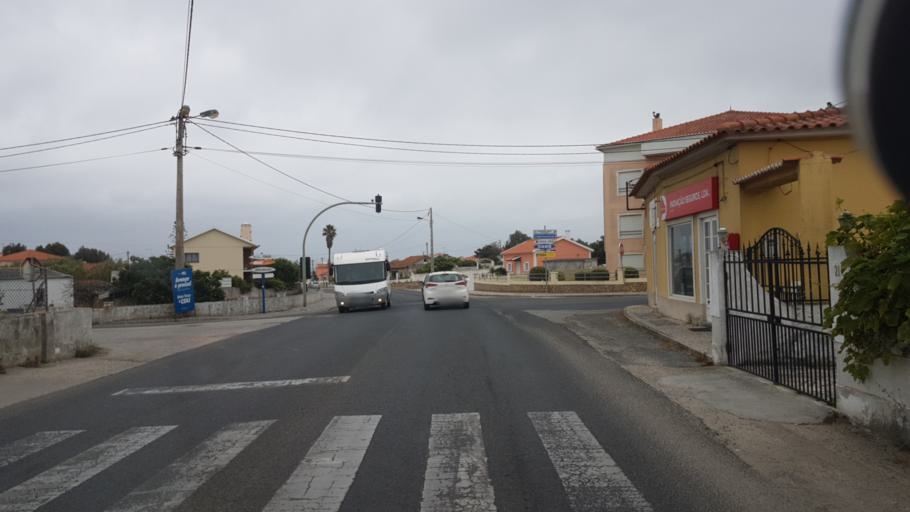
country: PT
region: Lisbon
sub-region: Torres Vedras
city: Silveira
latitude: 39.1197
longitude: -9.3749
